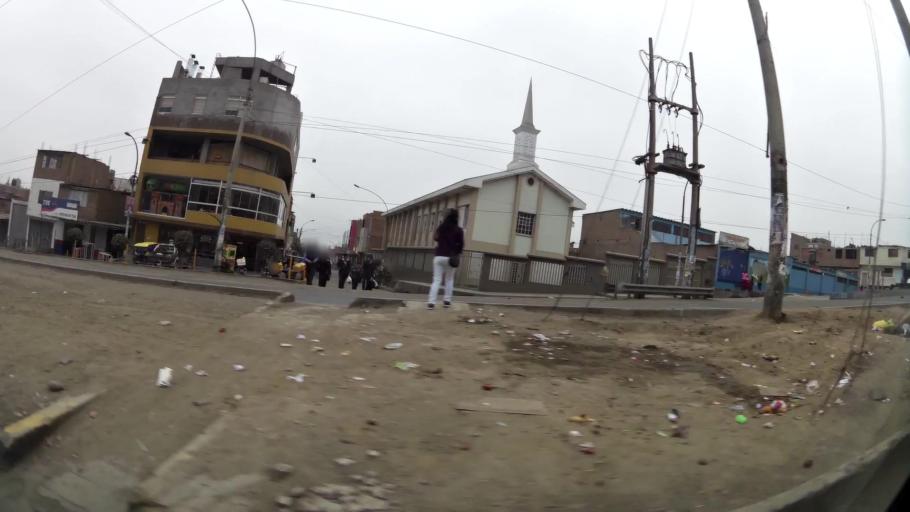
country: PE
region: Lima
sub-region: Lima
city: Urb. Santo Domingo
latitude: -11.8794
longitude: -77.0196
